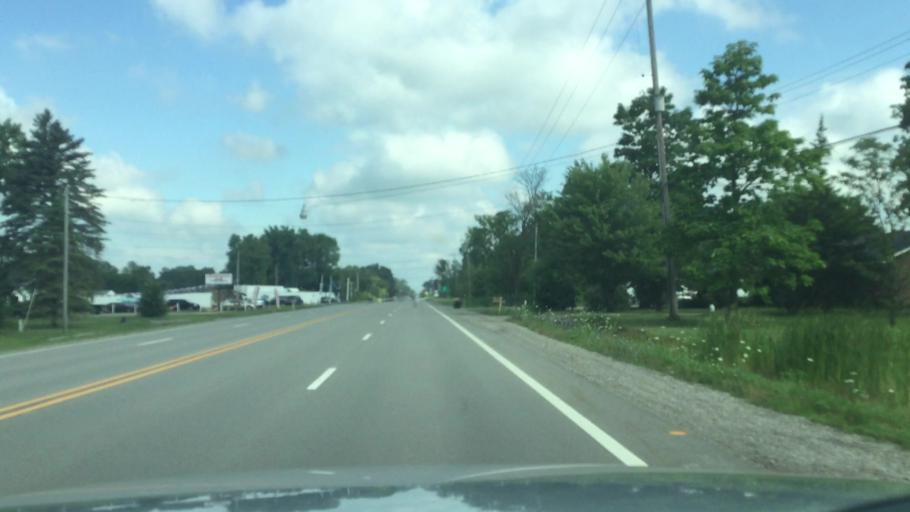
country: US
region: Michigan
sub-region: Genesee County
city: Clio
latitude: 43.1995
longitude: -83.7310
